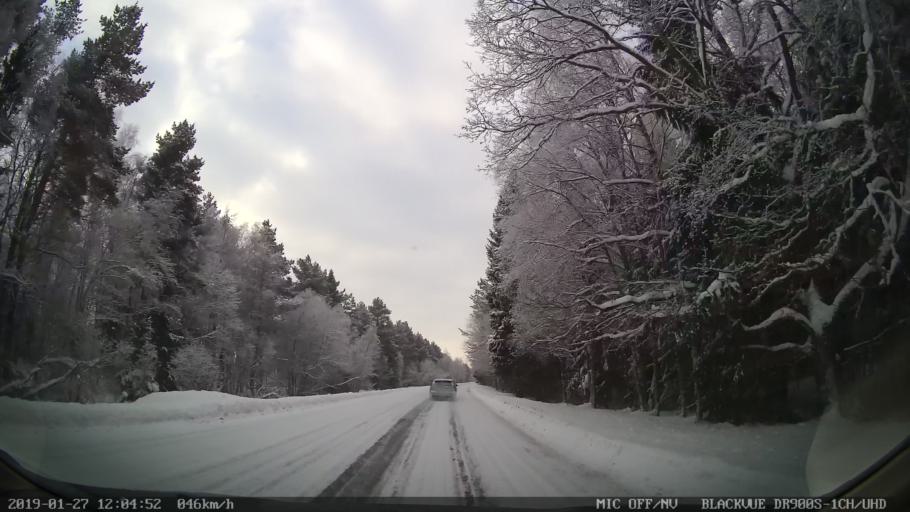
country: EE
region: Harju
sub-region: Raasiku vald
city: Raasiku
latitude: 59.4800
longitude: 25.2563
